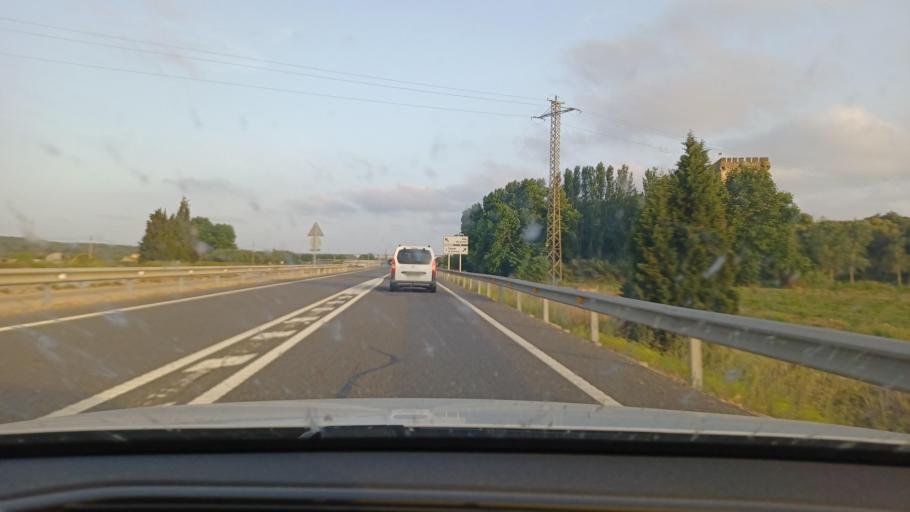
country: ES
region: Catalonia
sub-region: Provincia de Tarragona
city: Amposta
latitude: 40.7449
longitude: 0.5610
